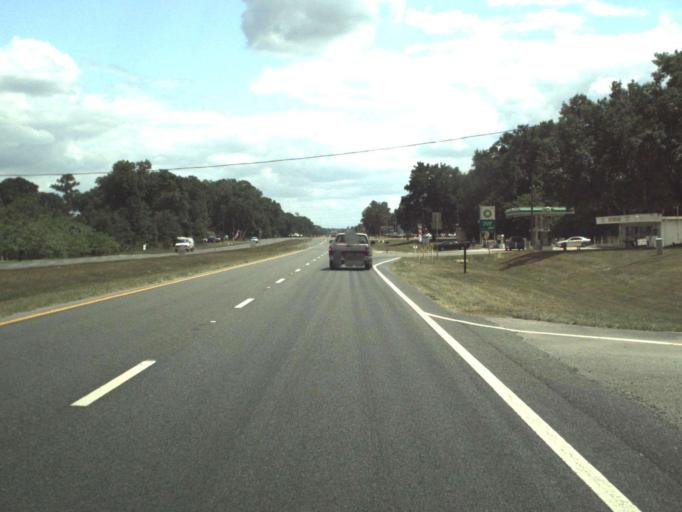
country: US
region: Florida
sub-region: Marion County
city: Ocala
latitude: 29.2338
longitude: -82.1509
